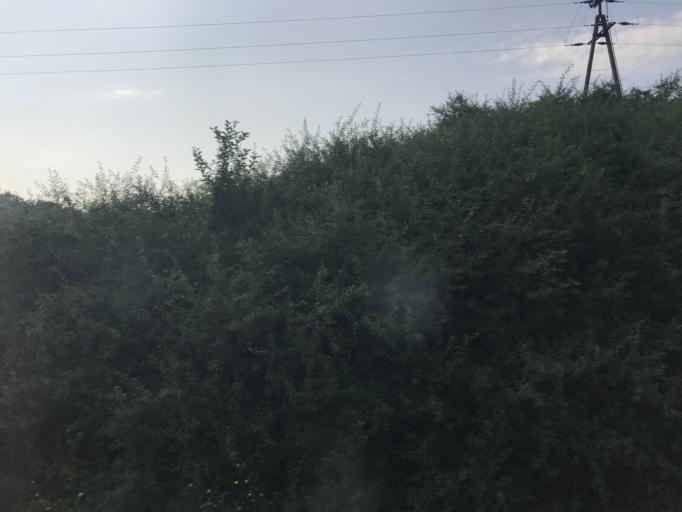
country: PL
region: Kujawsko-Pomorskie
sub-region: Powiat swiecki
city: Bukowiec
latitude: 53.3847
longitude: 18.3125
